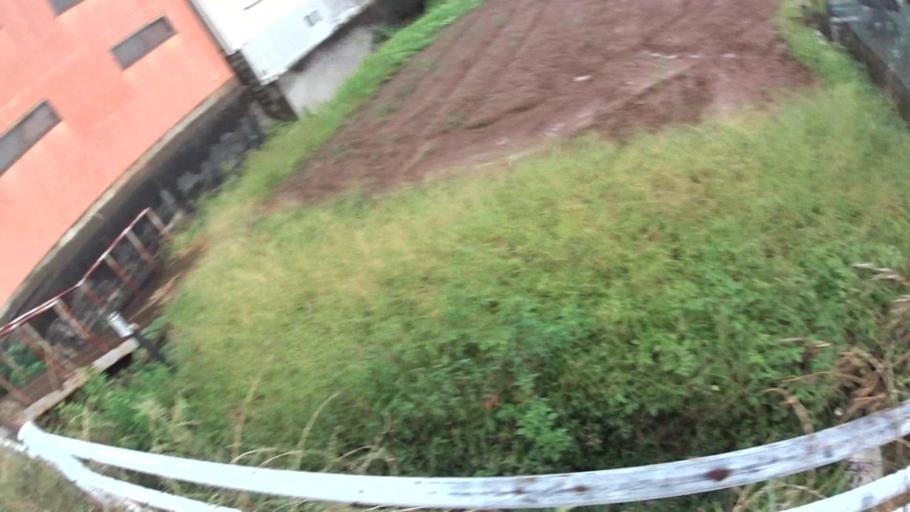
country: JP
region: Kyoto
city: Kyoto
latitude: 35.0090
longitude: 135.7117
